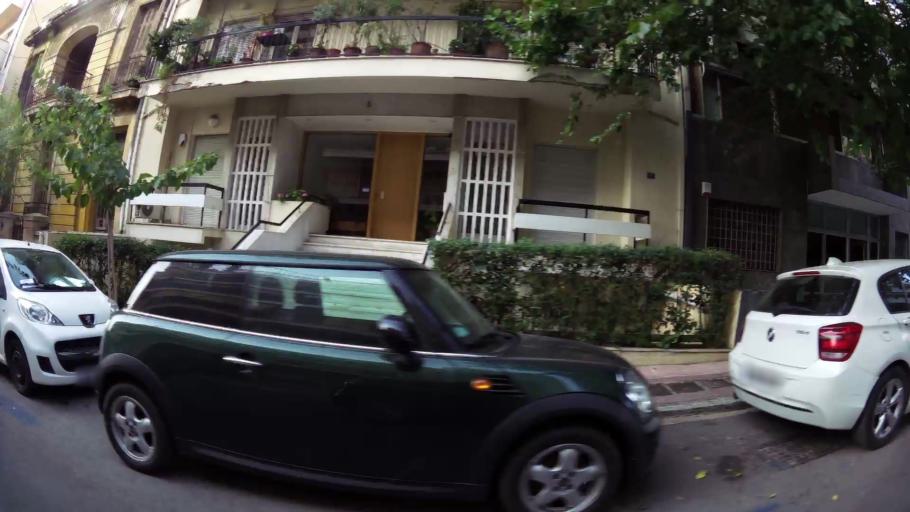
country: GR
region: Attica
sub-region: Nomarchia Athinas
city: Vyronas
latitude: 37.9795
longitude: 23.7491
